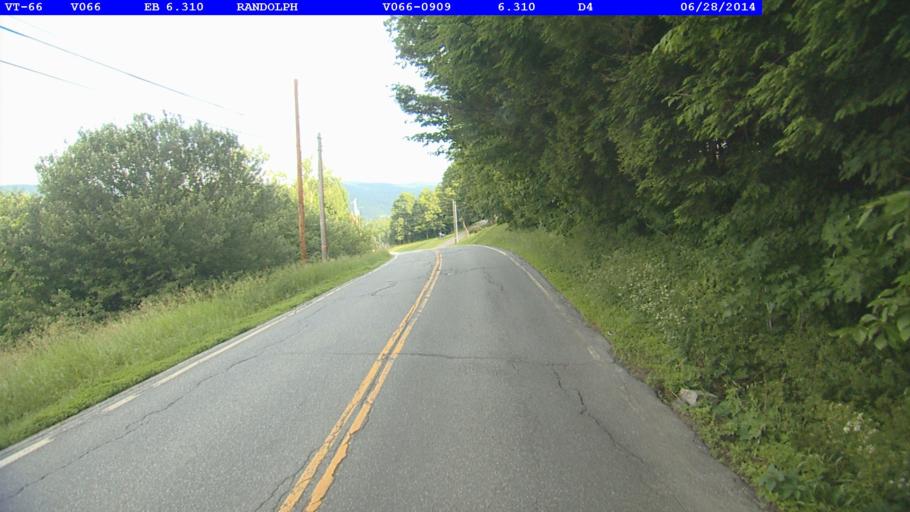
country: US
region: Vermont
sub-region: Orange County
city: Randolph
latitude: 43.9549
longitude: -72.5676
